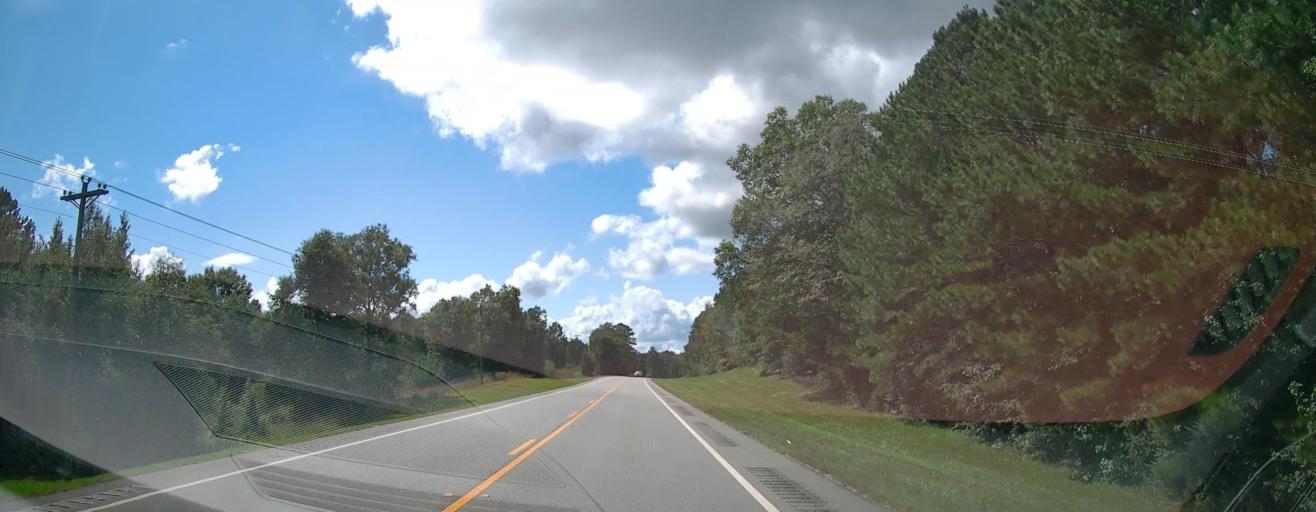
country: US
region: Georgia
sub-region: Baldwin County
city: Milledgeville
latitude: 33.0746
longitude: -83.3162
